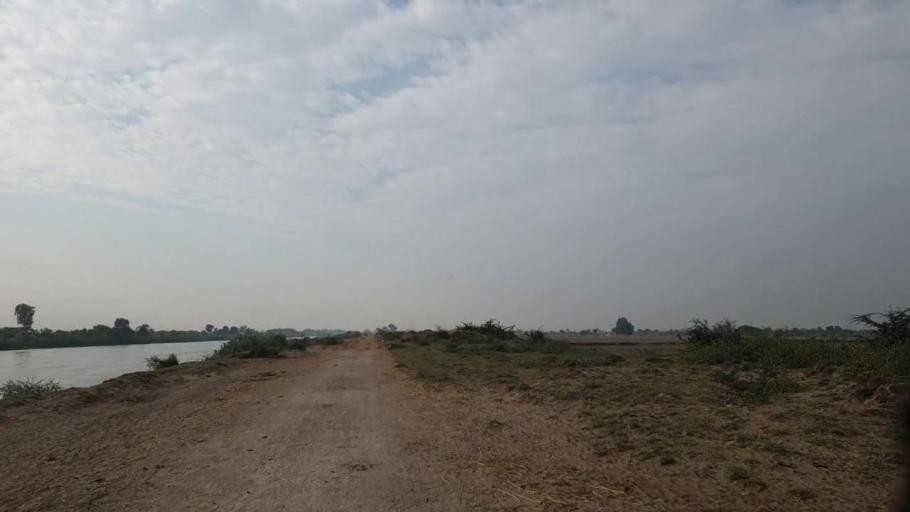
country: PK
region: Sindh
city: Tando Muhammad Khan
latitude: 25.0894
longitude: 68.4124
